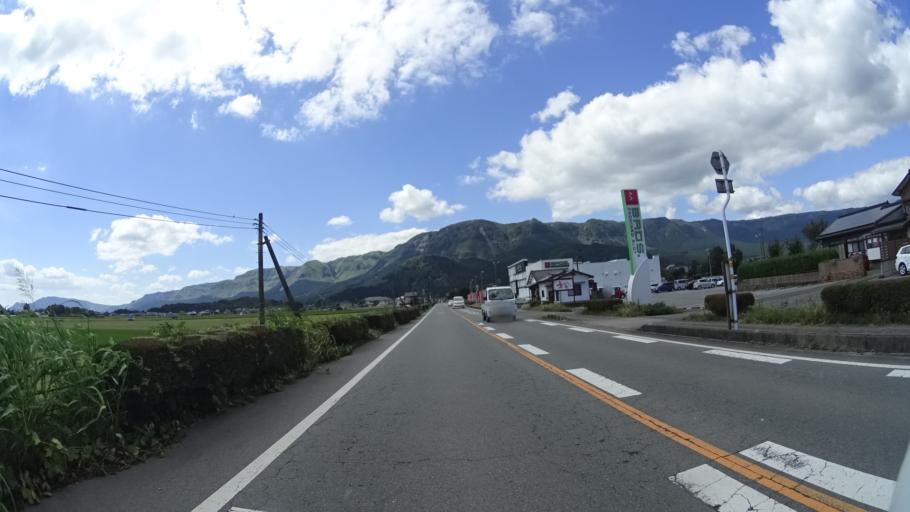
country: JP
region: Kumamoto
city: Aso
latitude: 32.9686
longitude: 131.0451
